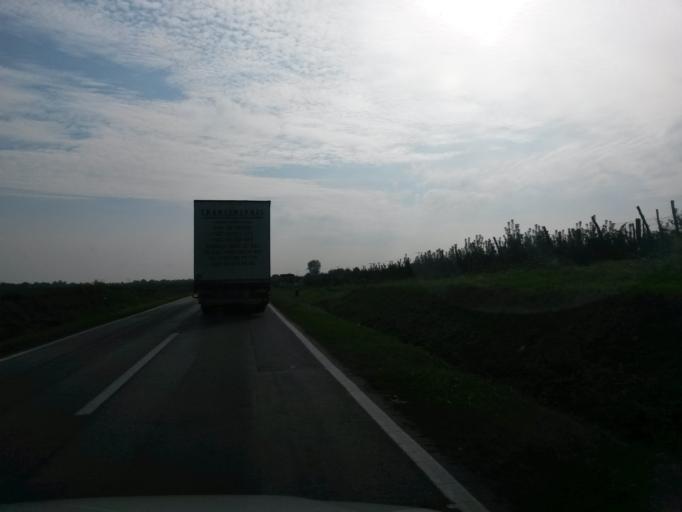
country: HR
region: Vukovarsko-Srijemska
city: Lovas
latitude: 45.2542
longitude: 19.1953
